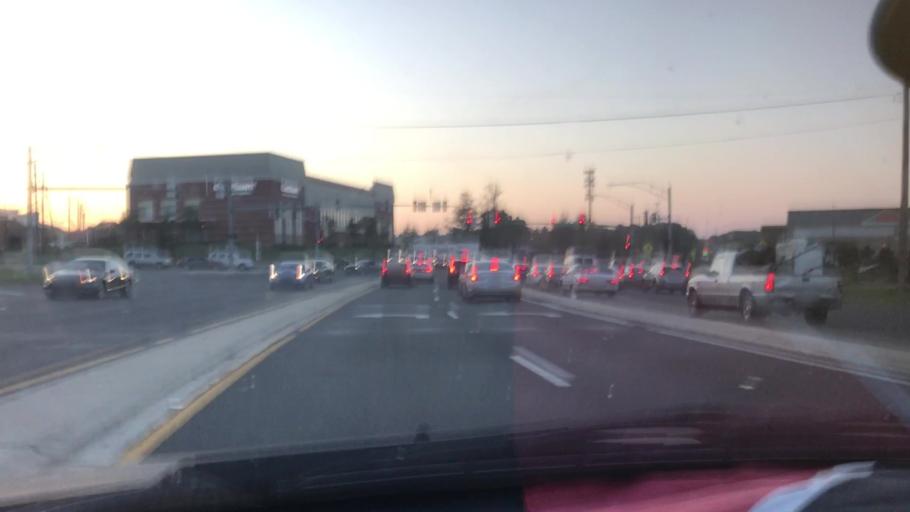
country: US
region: Maryland
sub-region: Prince George's County
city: Largo
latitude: 38.8691
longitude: -76.8494
